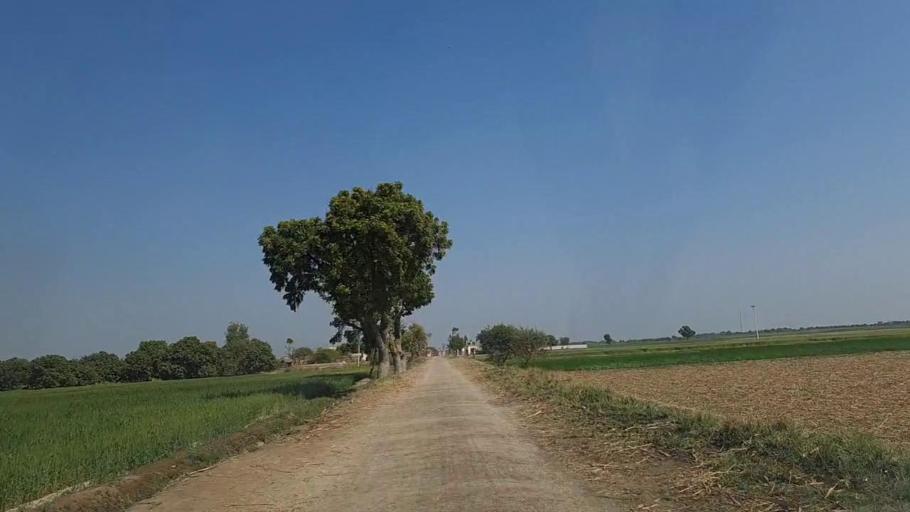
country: PK
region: Sindh
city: Digri
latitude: 25.2104
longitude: 69.1712
